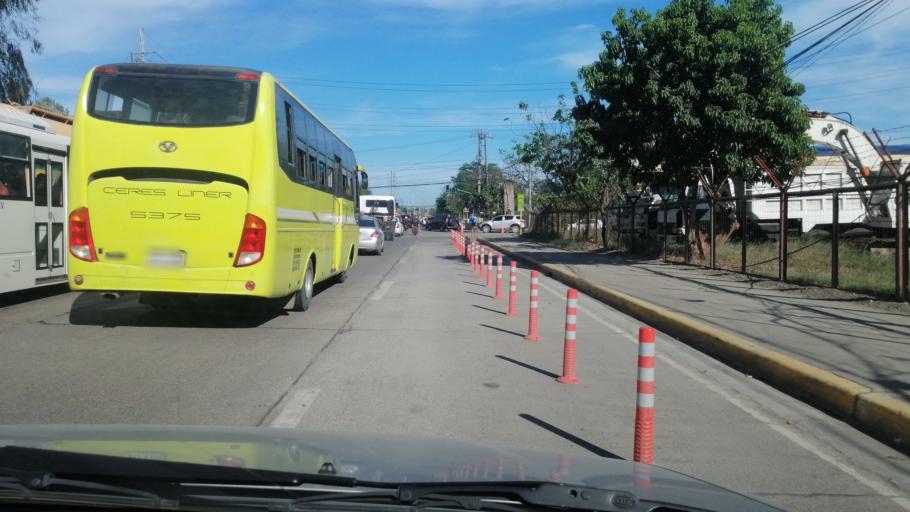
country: PH
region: Central Visayas
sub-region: Lapu-Lapu City
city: Buagsong
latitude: 10.3248
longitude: 123.9404
